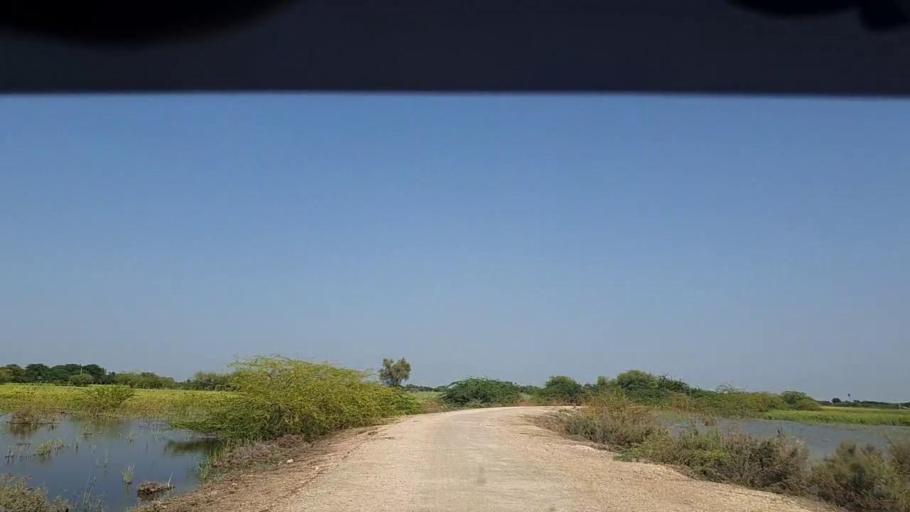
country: PK
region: Sindh
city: Badin
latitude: 24.4615
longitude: 68.7702
